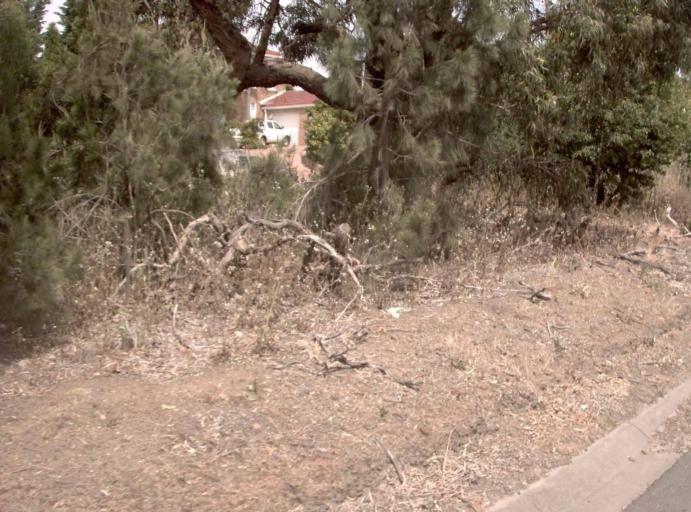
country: AU
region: Victoria
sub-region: Frankston
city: Frankston South
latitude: -38.1690
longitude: 145.1383
